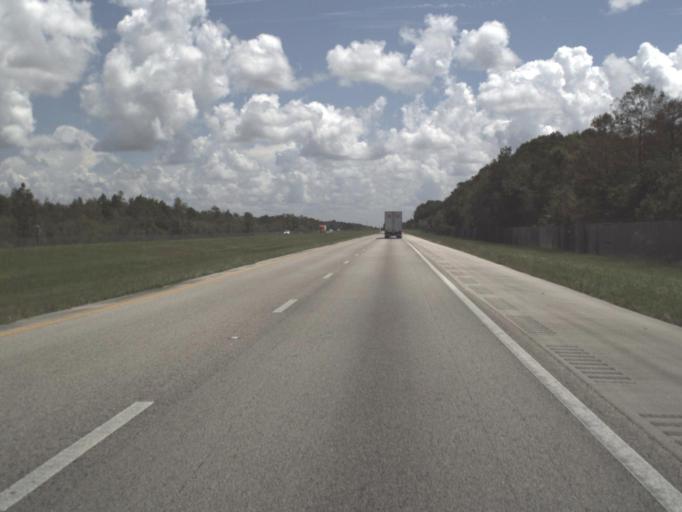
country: US
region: Florida
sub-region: Collier County
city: Orangetree
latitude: 26.1538
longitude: -81.3958
